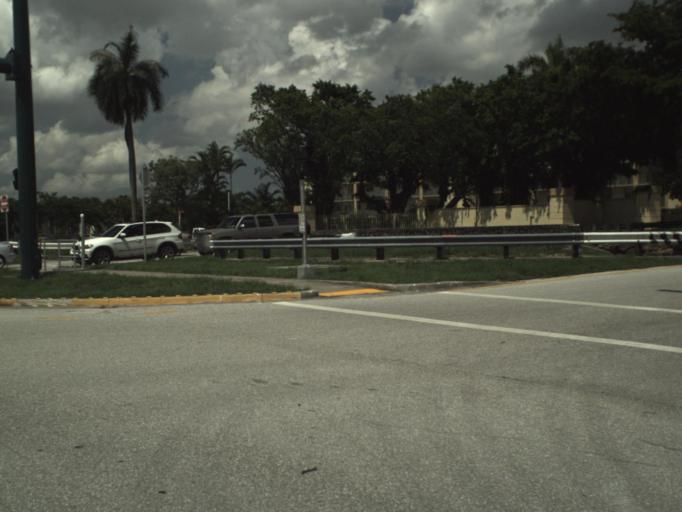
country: US
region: Florida
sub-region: Broward County
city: Parkland
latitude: 26.3357
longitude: -80.2030
